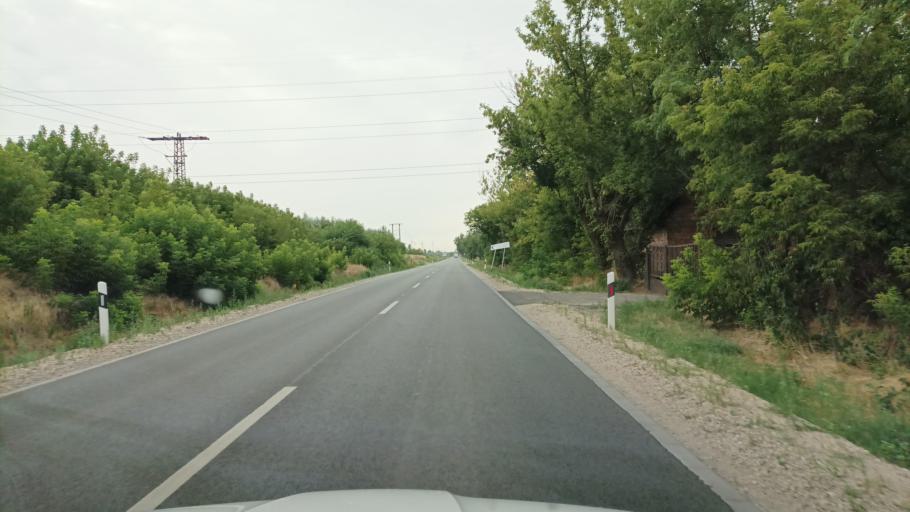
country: HU
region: Pest
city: Bugyi
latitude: 47.2307
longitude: 19.1803
